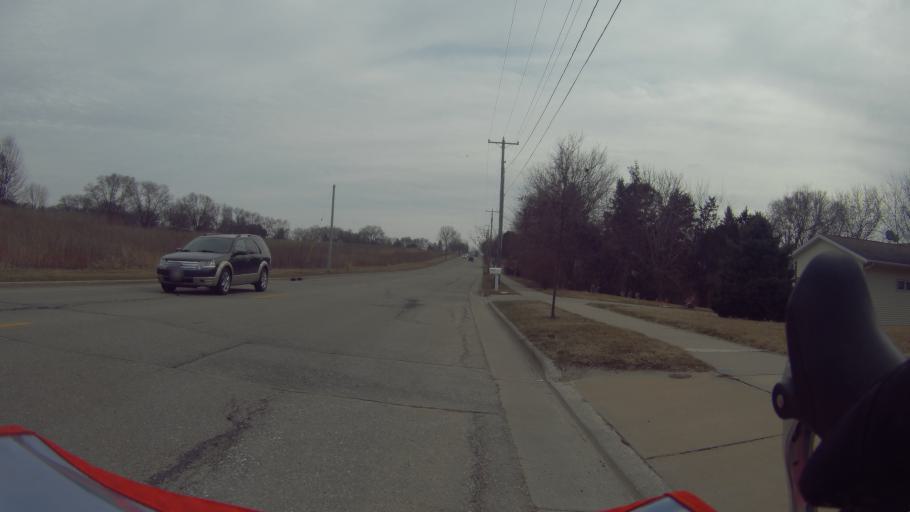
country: US
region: Wisconsin
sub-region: Dane County
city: Maple Bluff
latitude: 43.1389
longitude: -89.3978
